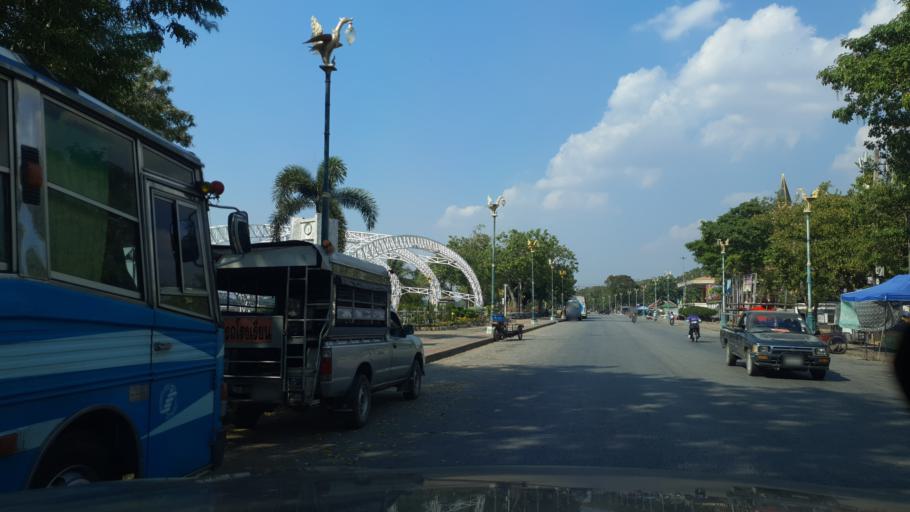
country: TH
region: Tak
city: Tak
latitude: 16.8768
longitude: 99.1213
